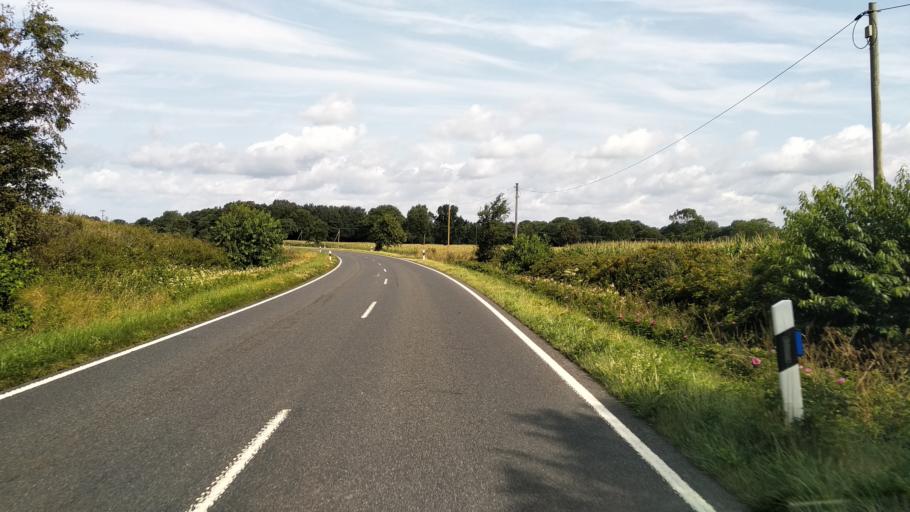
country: DE
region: Schleswig-Holstein
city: Lottorf
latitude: 54.4499
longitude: 9.5930
